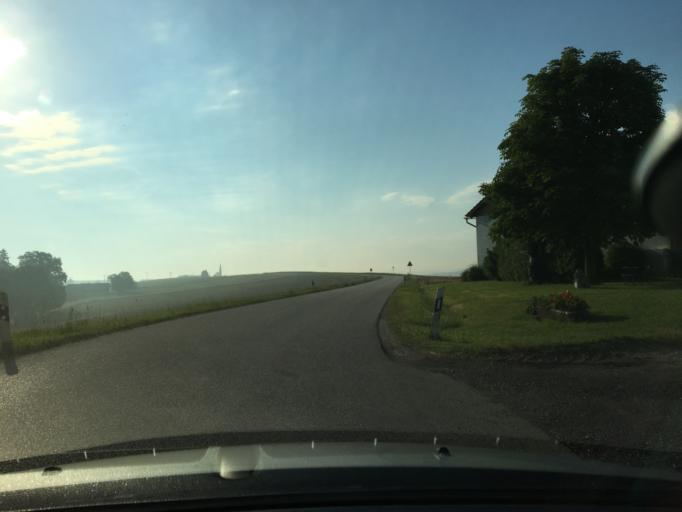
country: DE
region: Bavaria
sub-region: Lower Bavaria
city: Vilsbiburg
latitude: 48.4833
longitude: 12.3227
